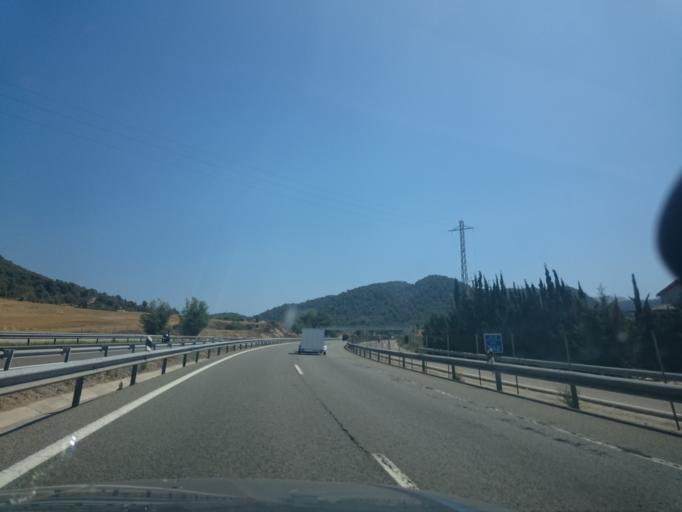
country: ES
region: Catalonia
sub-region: Provincia de Barcelona
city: Castelloli
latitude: 41.5983
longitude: 1.6976
